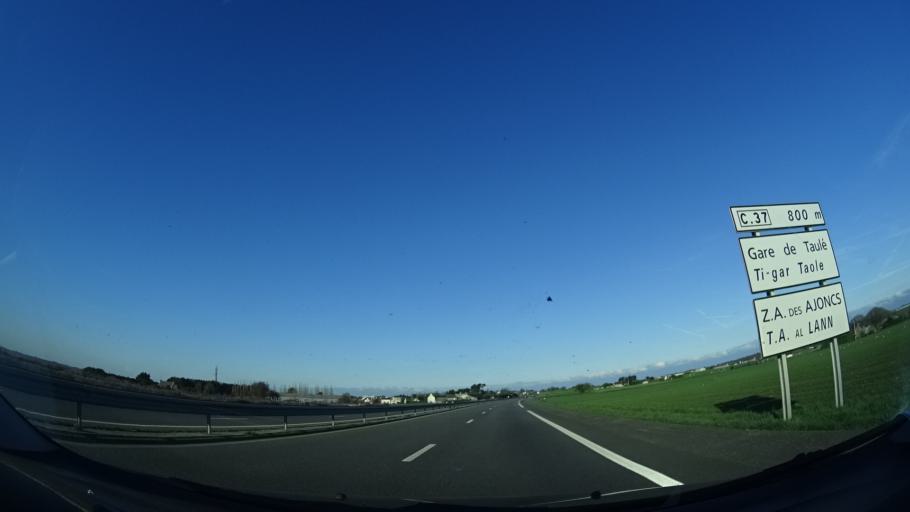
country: FR
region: Brittany
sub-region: Departement du Finistere
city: Taule
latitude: 48.6112
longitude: -3.8913
